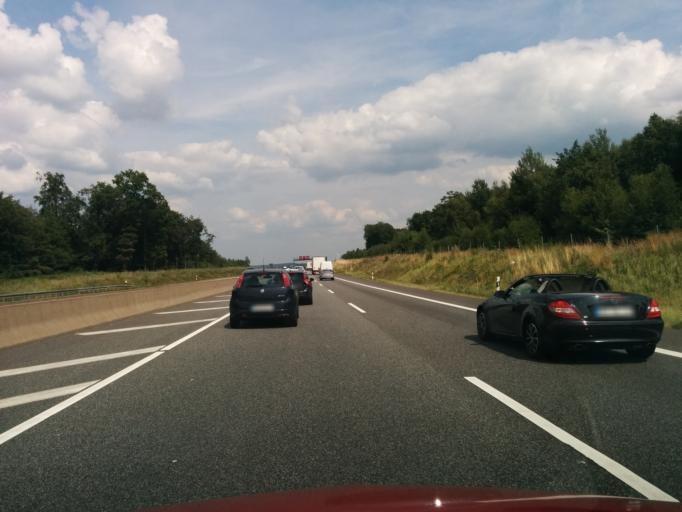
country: DE
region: Hesse
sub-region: Regierungsbezirk Giessen
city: Grunberg
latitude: 50.6494
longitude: 9.0041
